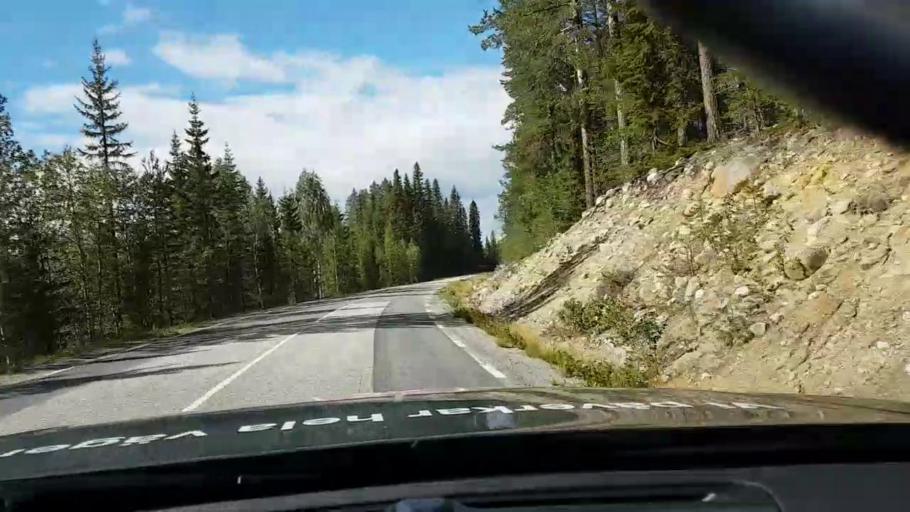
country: SE
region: Vaesterbotten
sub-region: Asele Kommun
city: Asele
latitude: 63.8362
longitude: 17.4375
